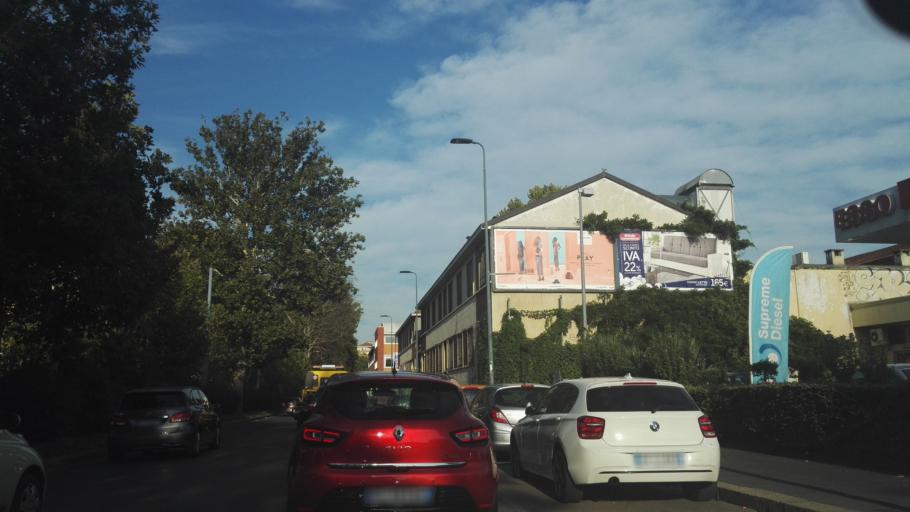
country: IT
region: Lombardy
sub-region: Citta metropolitana di Milano
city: Milano
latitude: 45.4439
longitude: 9.1686
